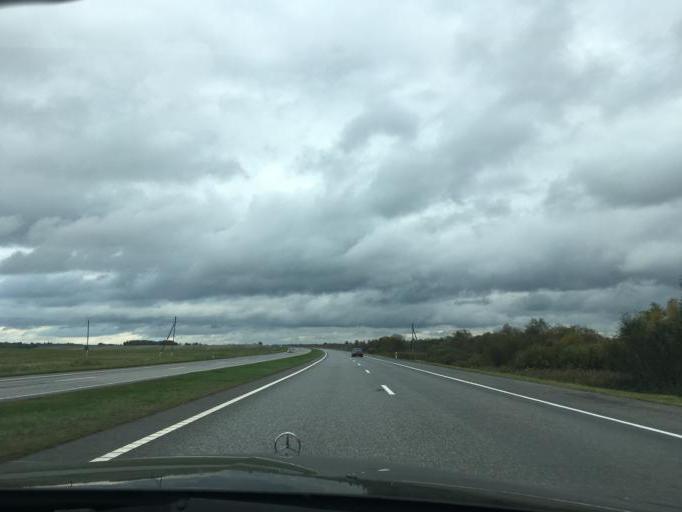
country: BY
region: Vitebsk
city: Kokhanava
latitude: 54.4735
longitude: 29.8908
